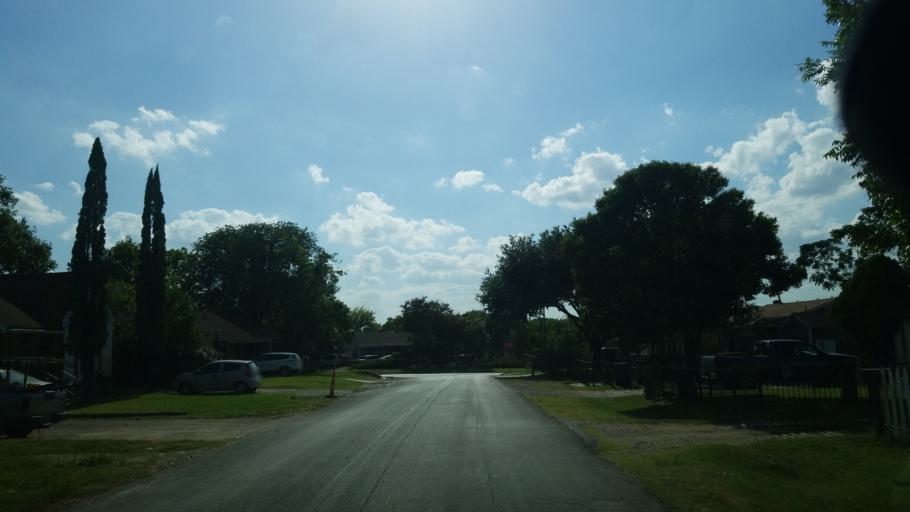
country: US
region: Texas
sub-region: Dallas County
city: Balch Springs
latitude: 32.7694
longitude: -96.7078
